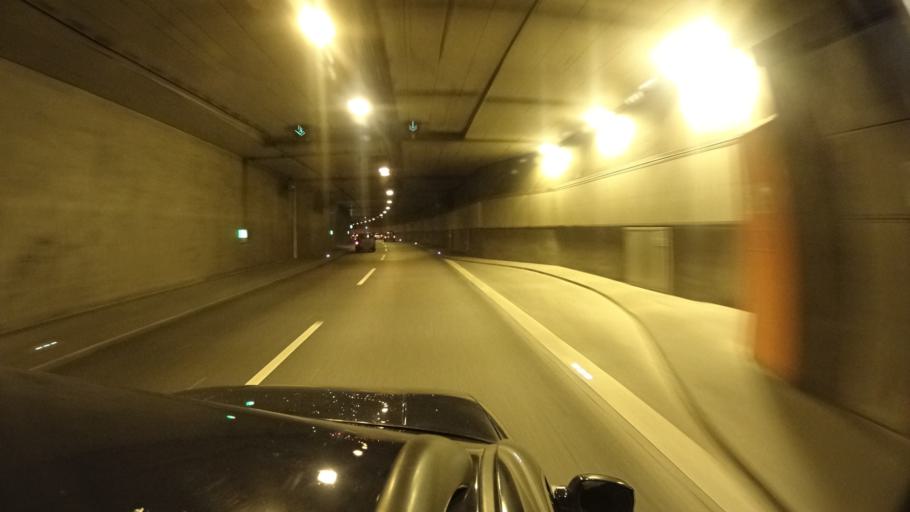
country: DE
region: Berlin
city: Tegel
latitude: 52.5592
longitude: 13.3107
